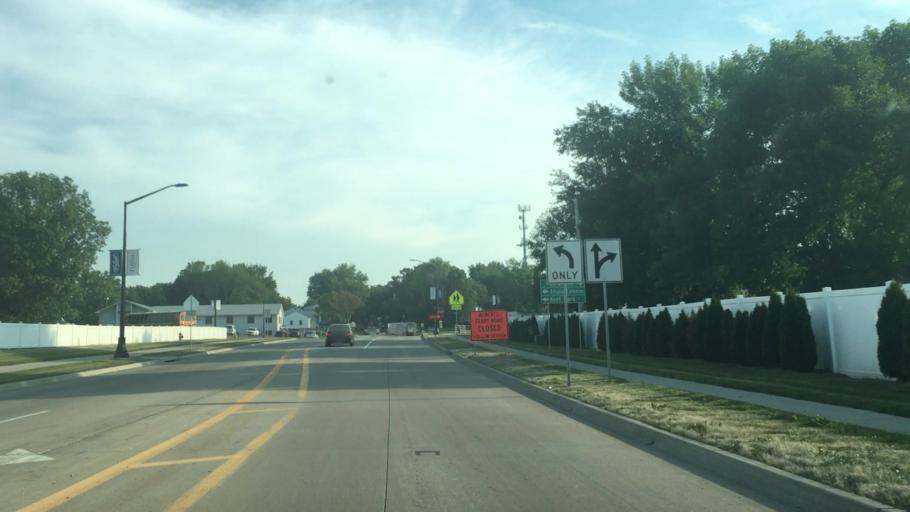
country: US
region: Iowa
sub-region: Johnson County
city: Tiffin
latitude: 41.7061
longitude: -91.6667
